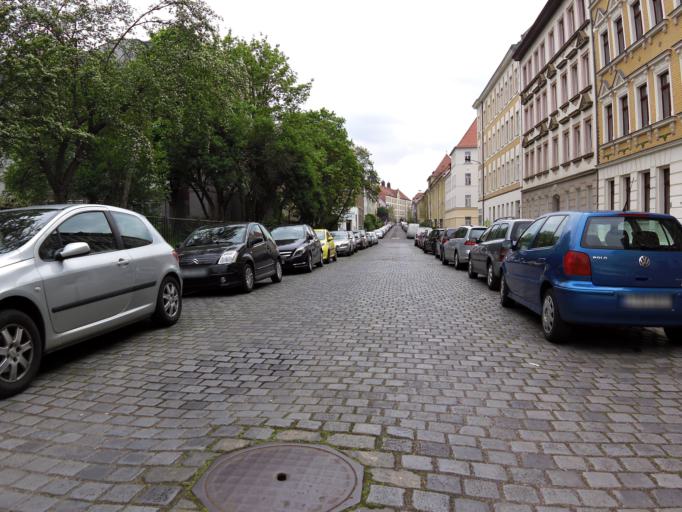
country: DE
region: Saxony
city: Markkleeberg
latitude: 51.3048
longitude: 12.3806
